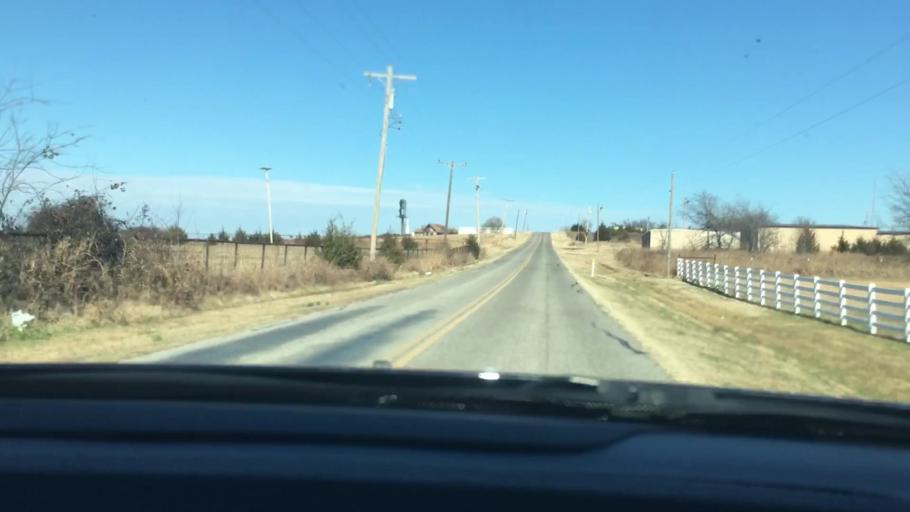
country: US
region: Oklahoma
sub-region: Murray County
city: Davis
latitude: 34.5016
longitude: -97.0553
